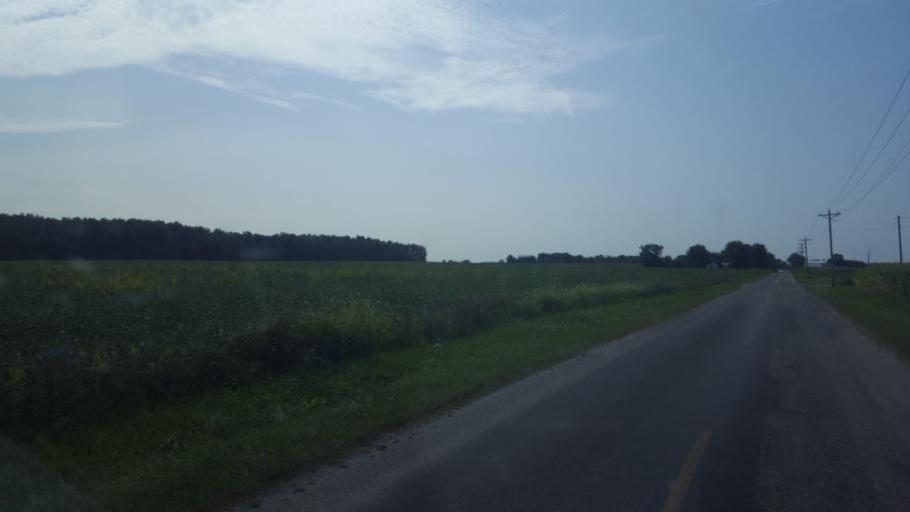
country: US
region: Ohio
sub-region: Morrow County
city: Cardington
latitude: 40.5100
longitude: -82.9955
